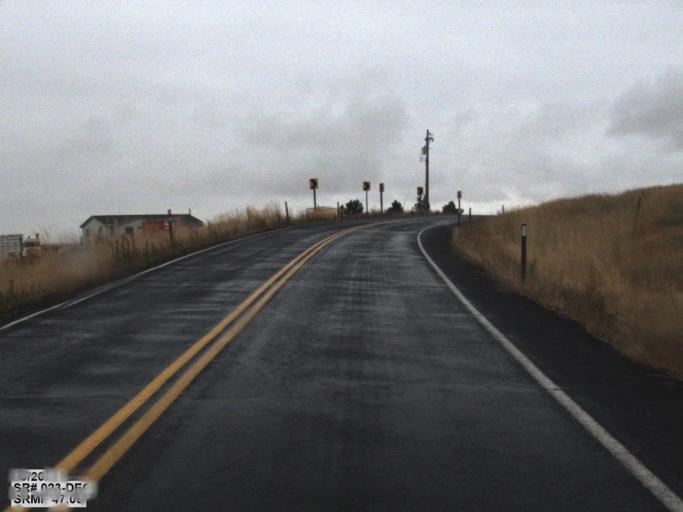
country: US
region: Washington
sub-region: Lincoln County
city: Davenport
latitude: 47.3425
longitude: -118.0057
